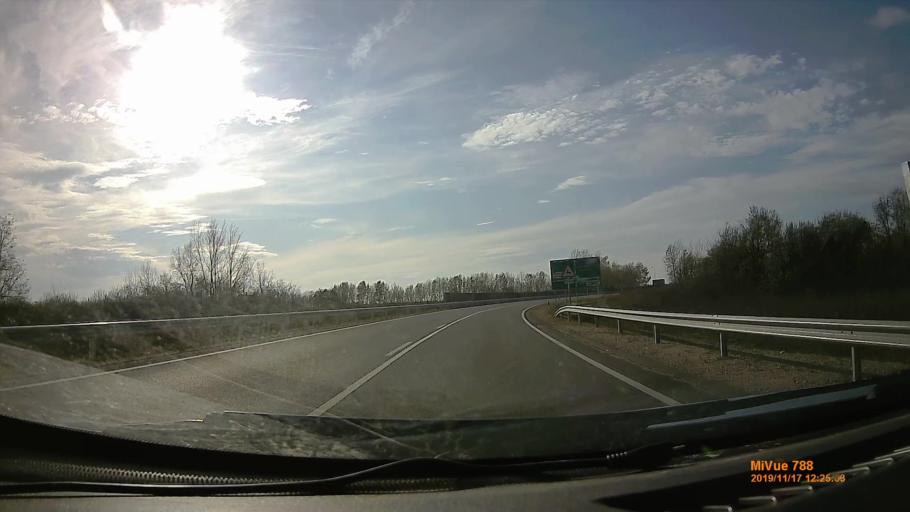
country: HU
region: Bacs-Kiskun
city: Kecskemet
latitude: 46.9323
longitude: 19.6367
